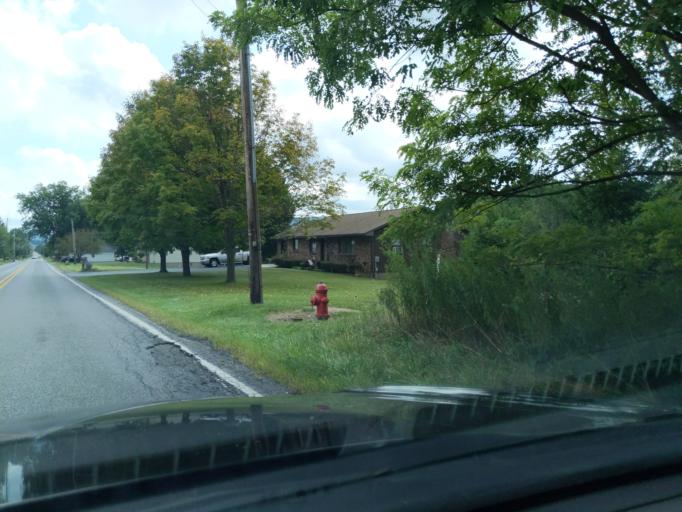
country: US
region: Pennsylvania
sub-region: Blair County
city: Duncansville
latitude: 40.3901
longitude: -78.4551
